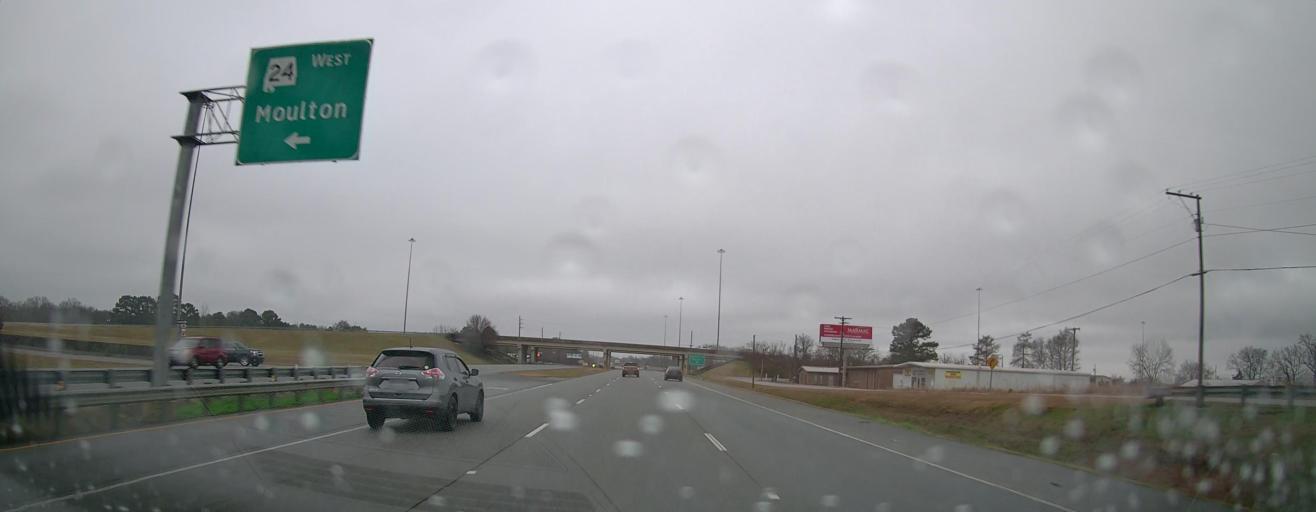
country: US
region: Alabama
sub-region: Morgan County
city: Decatur
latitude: 34.6039
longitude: -87.0314
